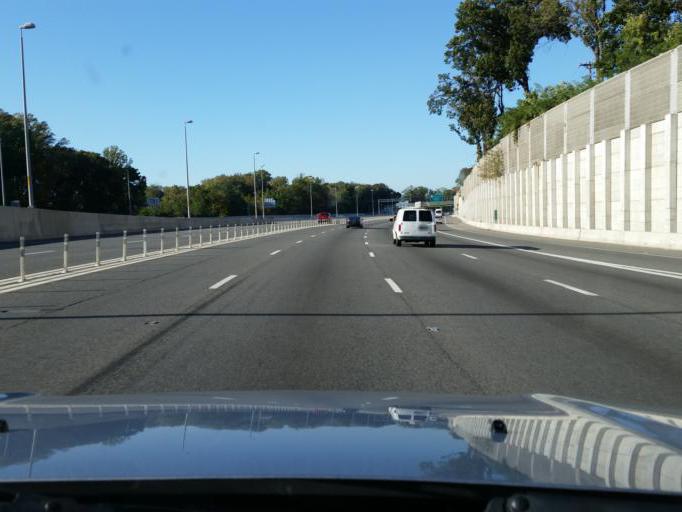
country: US
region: Virginia
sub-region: Fairfax County
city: Ravensworth
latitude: 38.8153
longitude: -77.2204
